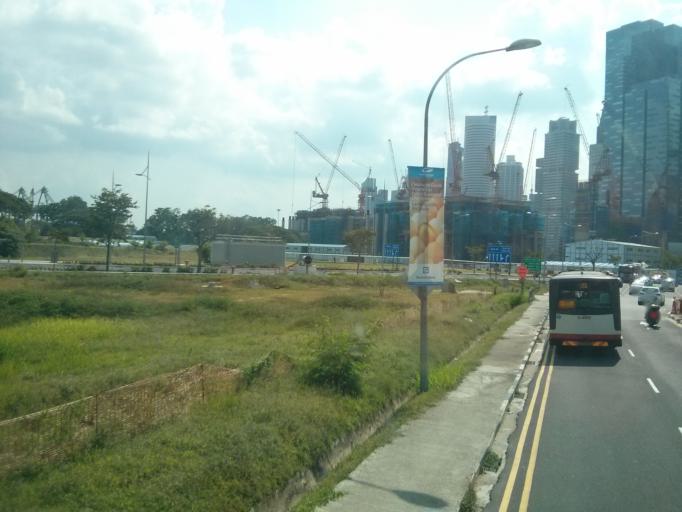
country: SG
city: Singapore
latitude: 1.2781
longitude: 103.8560
